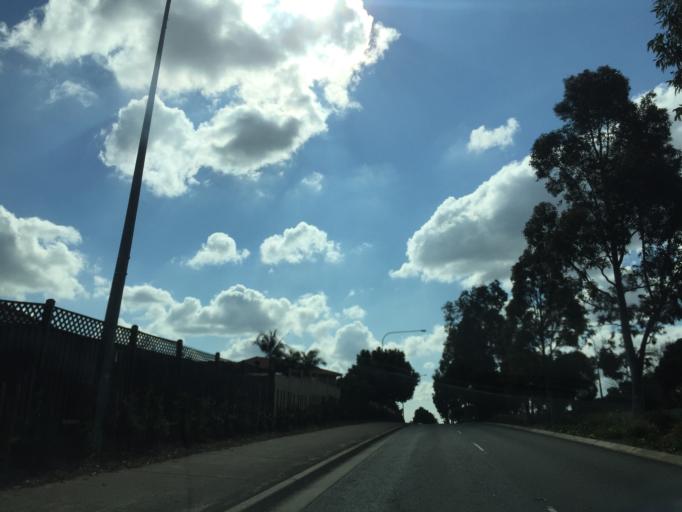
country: AU
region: New South Wales
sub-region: Blacktown
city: Quakers Hill
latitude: -33.7152
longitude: 150.8928
